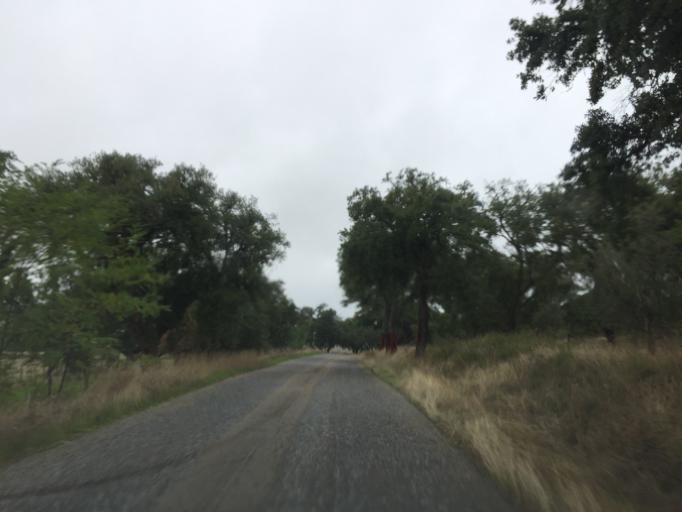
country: PT
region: Portalegre
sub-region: Alter do Chao
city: Alter do Chao
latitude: 39.2367
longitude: -7.6529
